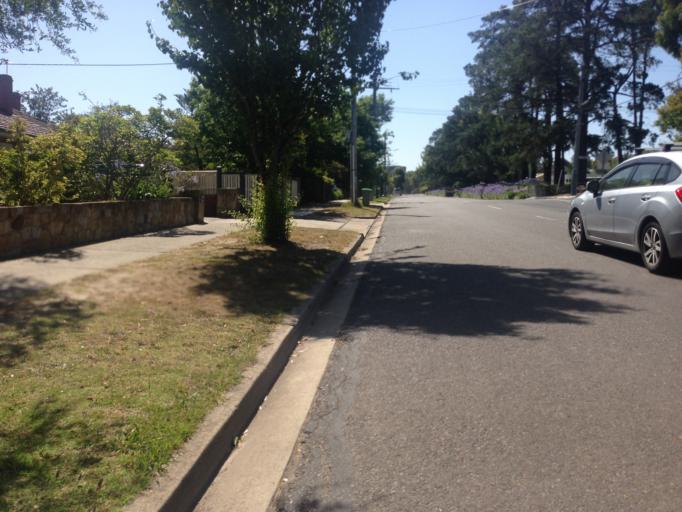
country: AU
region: Victoria
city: Ivanhoe East
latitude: -37.7748
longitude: 145.0526
